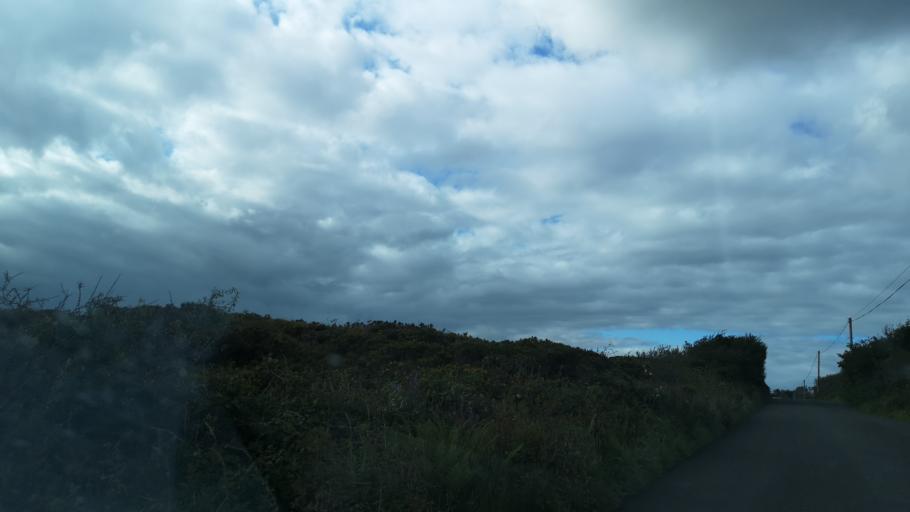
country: IE
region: Connaught
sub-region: County Galway
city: Bearna
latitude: 53.2721
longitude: -9.1597
